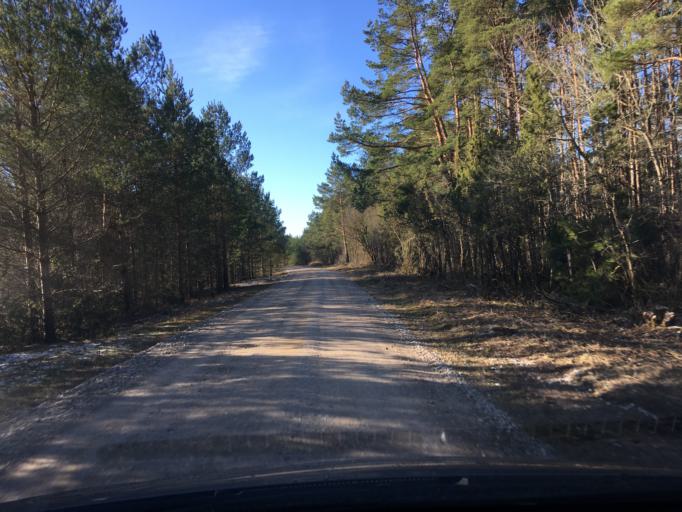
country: EE
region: Laeaene
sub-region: Lihula vald
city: Lihula
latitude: 58.5795
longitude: 23.7031
